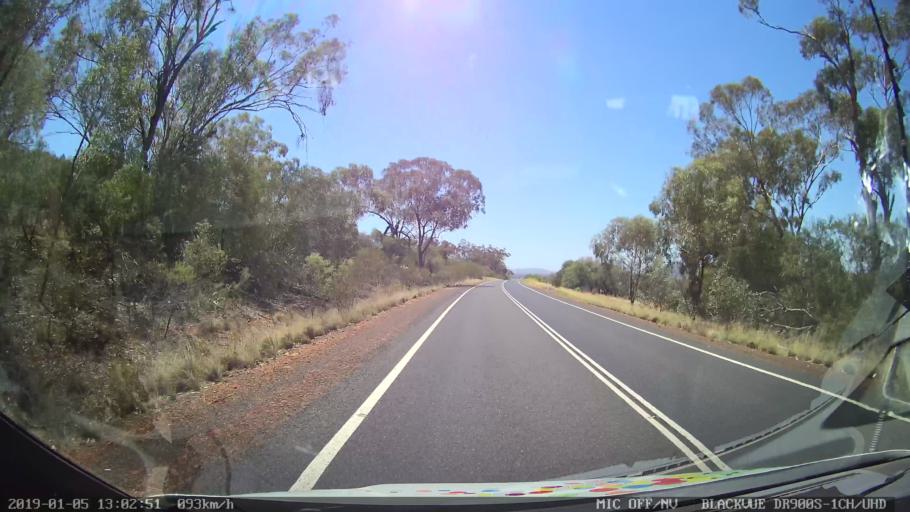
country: AU
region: New South Wales
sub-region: Gunnedah
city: Gunnedah
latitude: -31.1129
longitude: 149.8180
